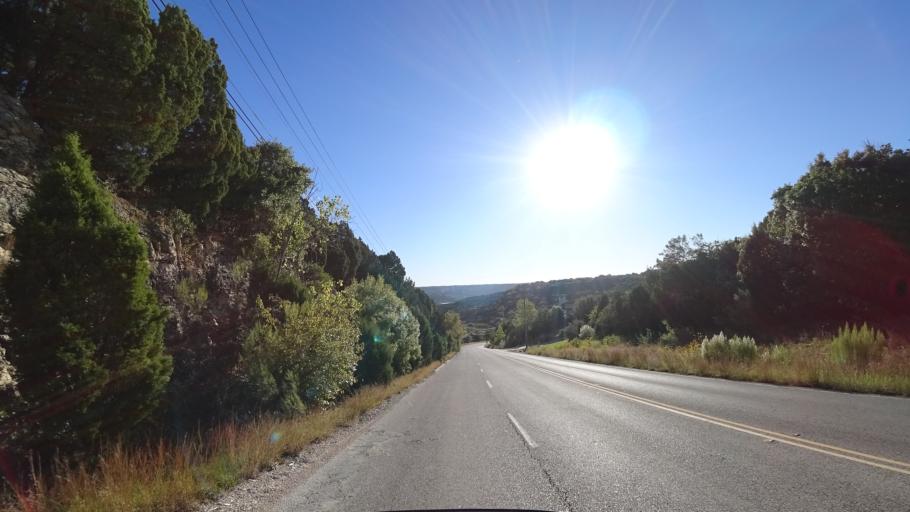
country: US
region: Texas
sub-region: Travis County
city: West Lake Hills
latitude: 30.3640
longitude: -97.8065
